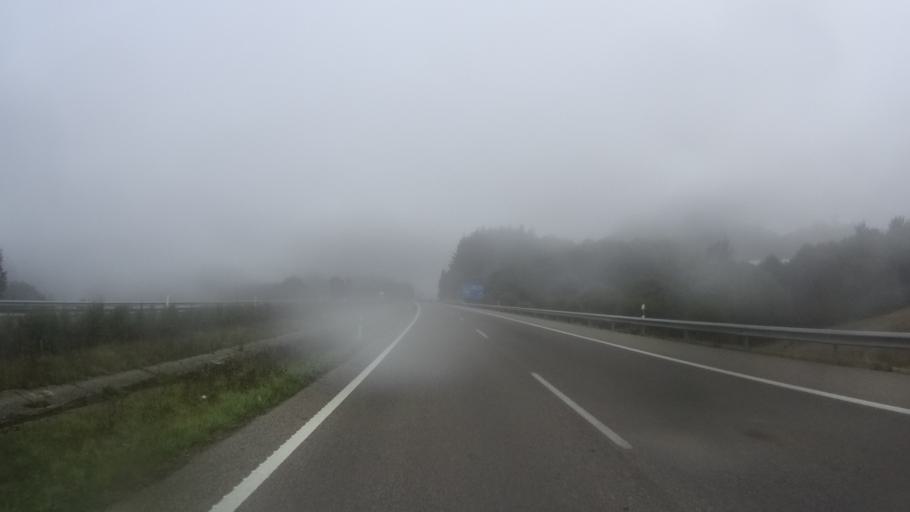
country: ES
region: Galicia
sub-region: Provincia de Lugo
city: Guitiriz
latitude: 43.1787
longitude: -7.8052
